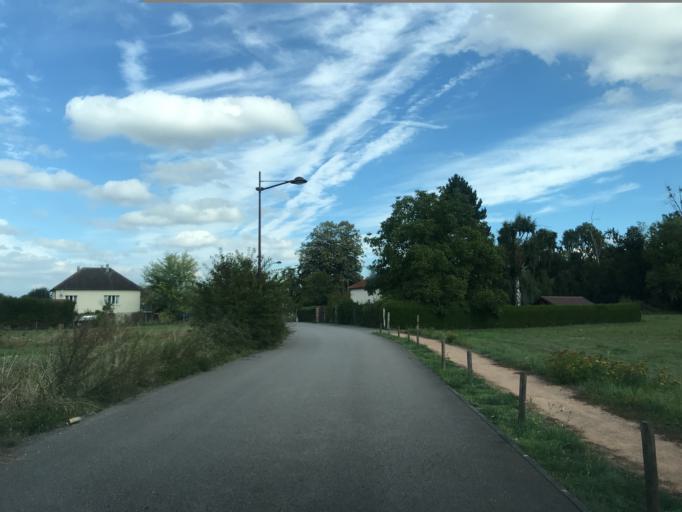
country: FR
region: Haute-Normandie
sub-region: Departement de l'Eure
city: Le Vaudreuil
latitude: 49.2500
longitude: 1.1918
